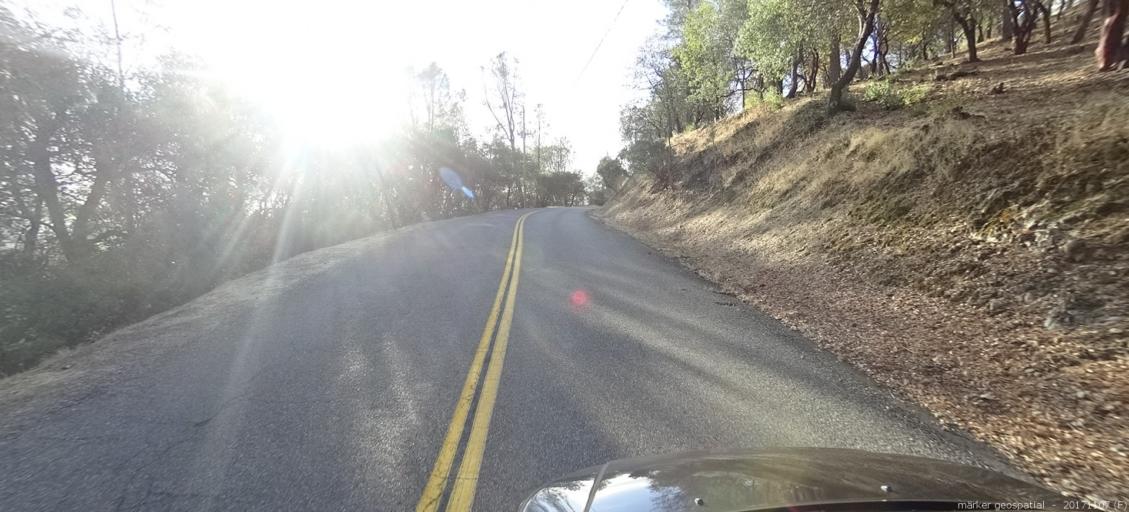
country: US
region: California
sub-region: Shasta County
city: Shasta
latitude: 40.5878
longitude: -122.4669
